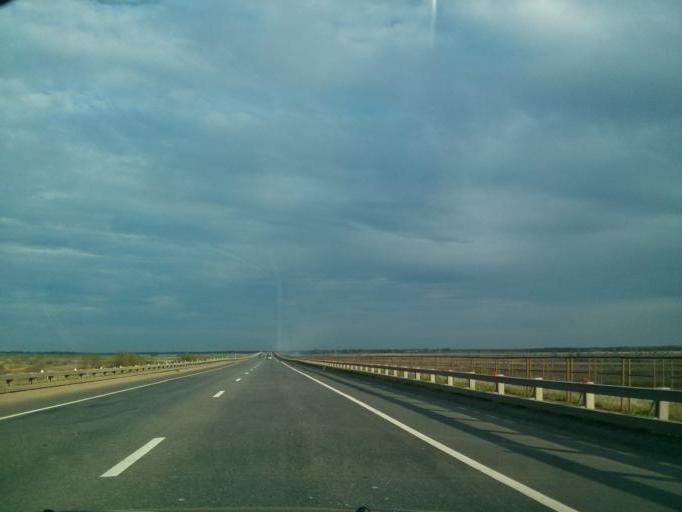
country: RU
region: Vladimir
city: Murom
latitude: 55.5997
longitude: 42.1022
